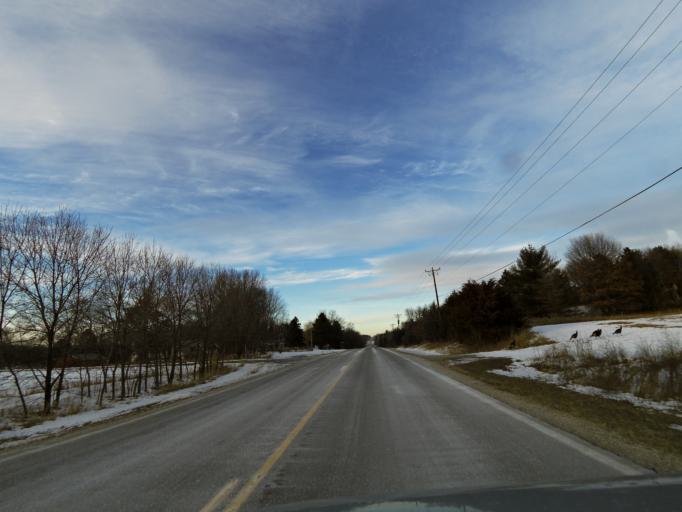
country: US
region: Minnesota
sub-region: Washington County
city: Afton
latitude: 44.9011
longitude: -92.8429
